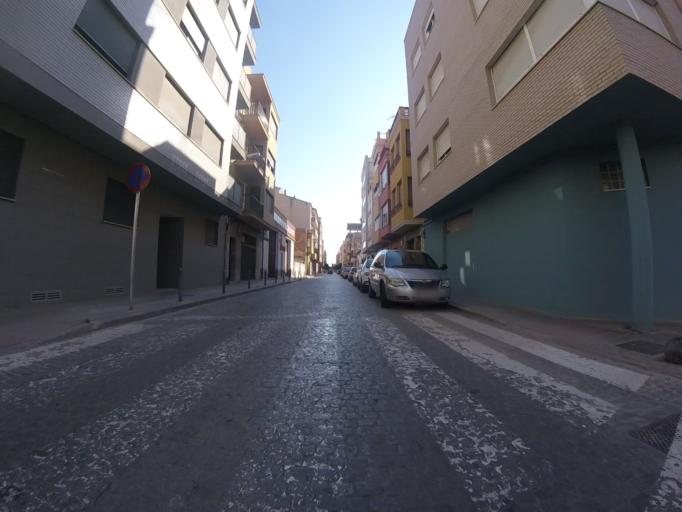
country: ES
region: Valencia
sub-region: Provincia de Castello
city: Benicarlo
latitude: 40.4210
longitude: 0.4269
